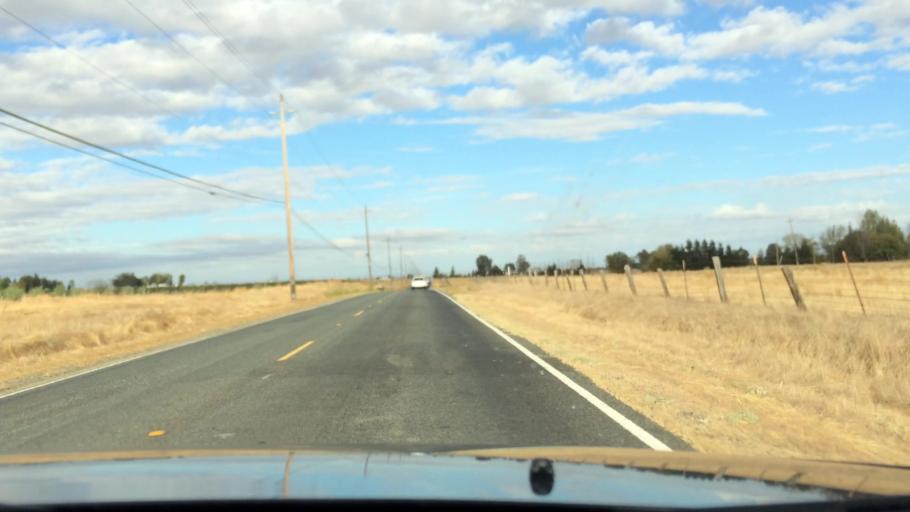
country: US
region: California
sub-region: Sacramento County
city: Herald
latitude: 38.3114
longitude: -121.2161
